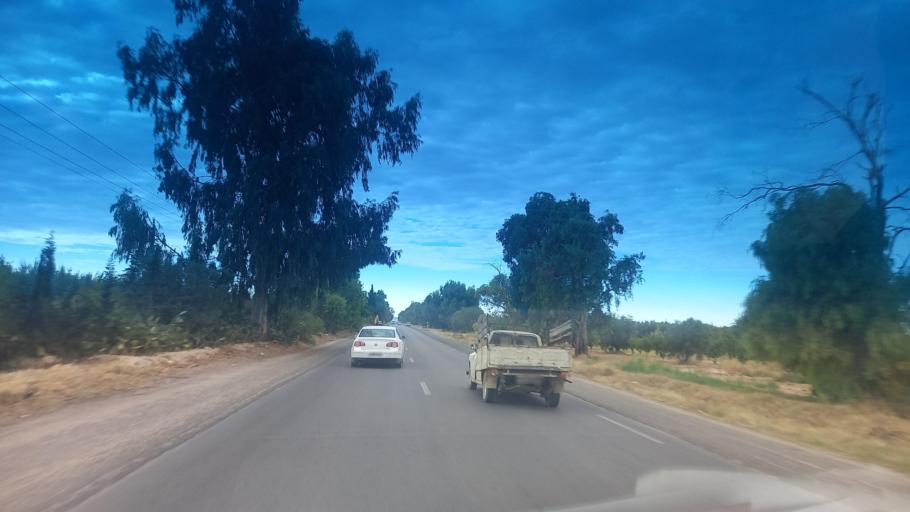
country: TN
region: Al Qasrayn
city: Sbiba
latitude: 35.2983
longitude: 9.0891
